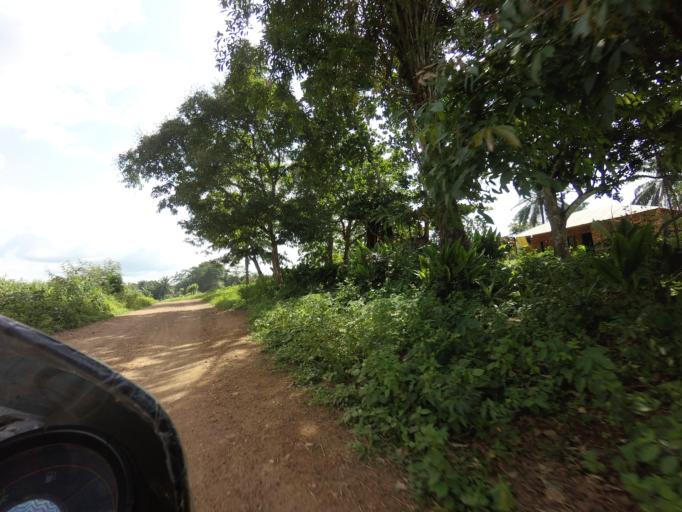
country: SL
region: Eastern Province
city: Daru
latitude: 8.0528
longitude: -10.8352
